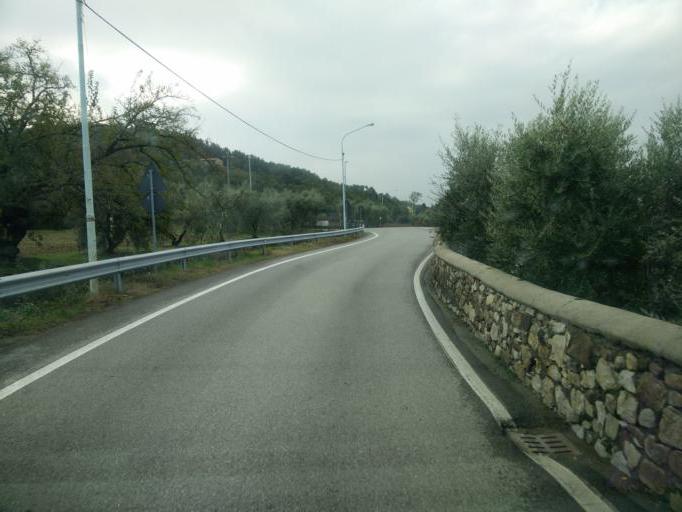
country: IT
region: Tuscany
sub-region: Provincia di Prato
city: Prato
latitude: 43.9167
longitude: 11.0952
